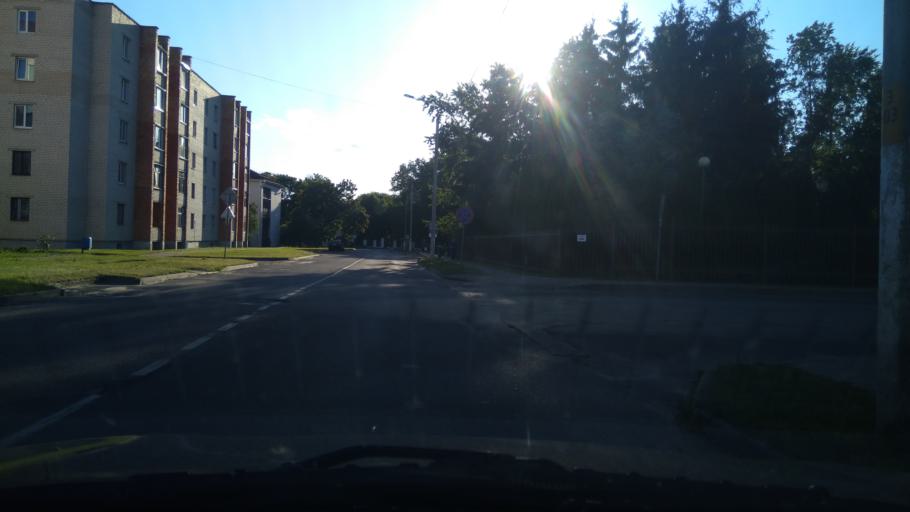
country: BY
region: Brest
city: Pruzhany
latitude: 52.5642
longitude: 24.4595
